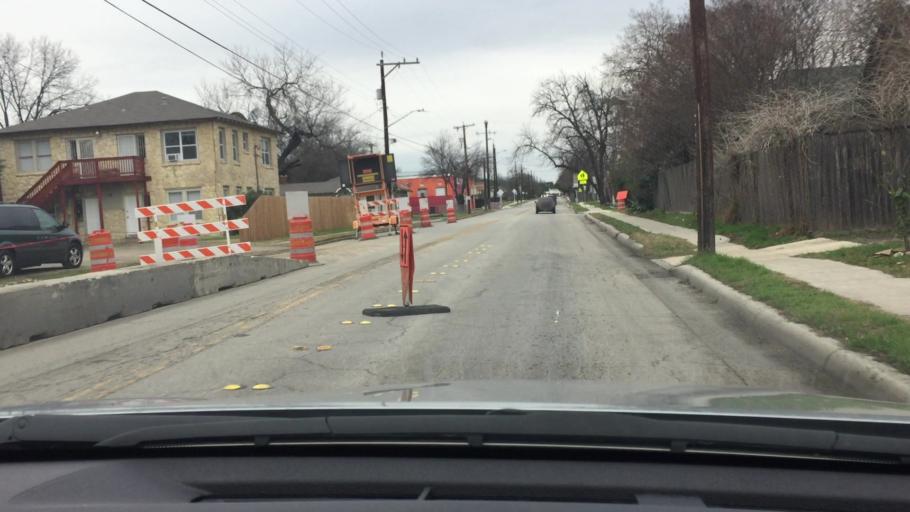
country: US
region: Texas
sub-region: Bexar County
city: San Antonio
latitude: 29.4543
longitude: -98.5238
